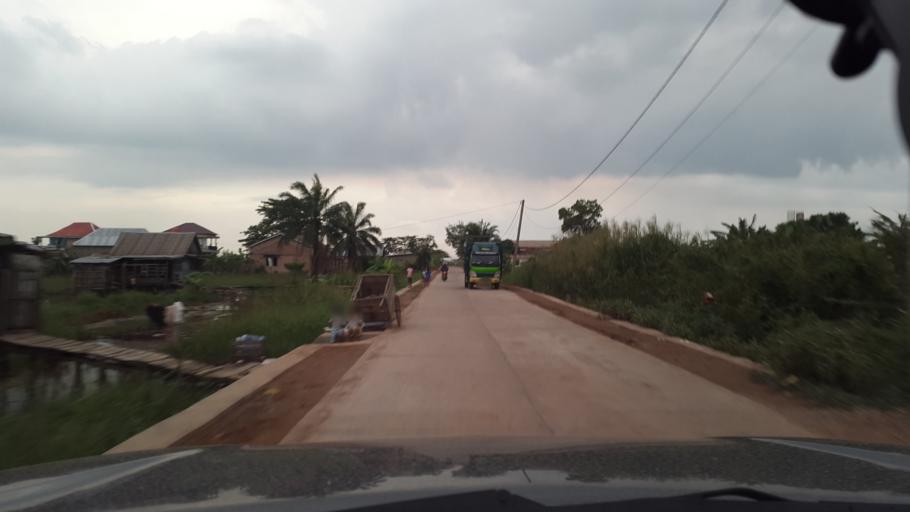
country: ID
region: South Sumatra
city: Plaju
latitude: -3.0573
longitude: 104.7892
